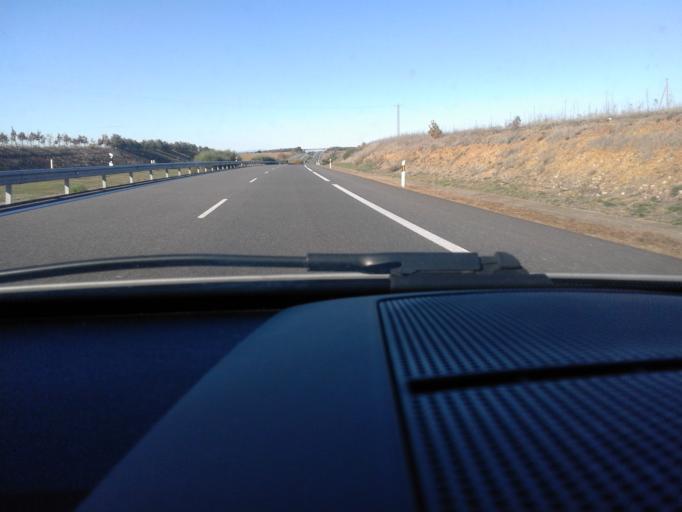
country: ES
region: Castille and Leon
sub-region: Provincia de Leon
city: Villamoratiel de las Matas
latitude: 42.4223
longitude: -5.2854
